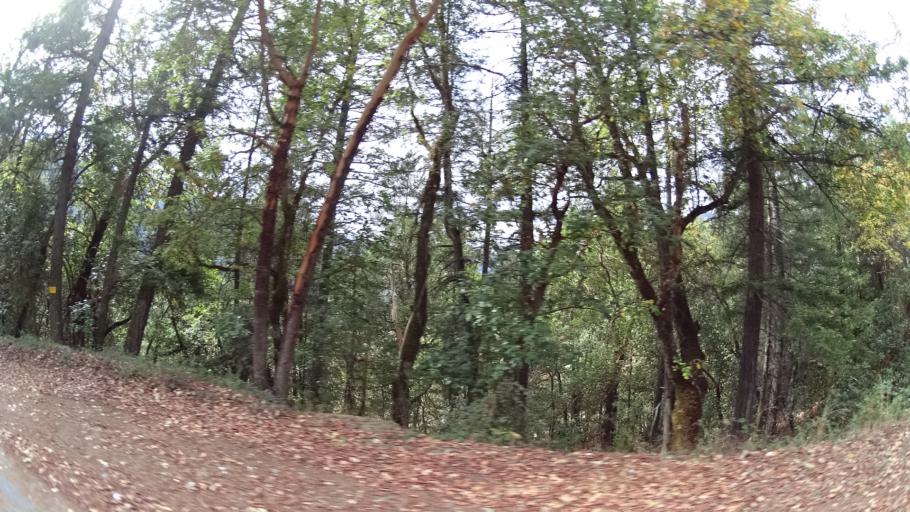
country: US
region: California
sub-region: Siskiyou County
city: Happy Camp
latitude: 41.7899
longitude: -123.3053
